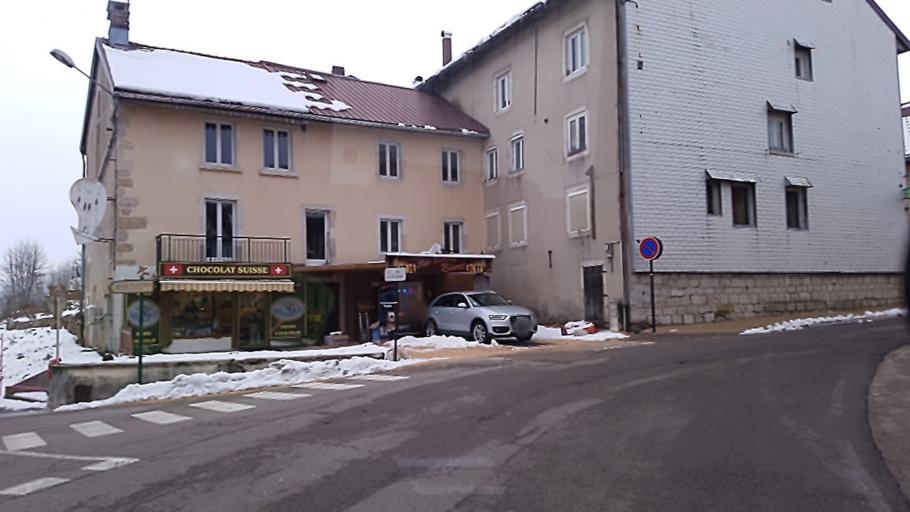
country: FR
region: Franche-Comte
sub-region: Departement du Jura
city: Les Rousses
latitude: 46.4863
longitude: 6.0599
